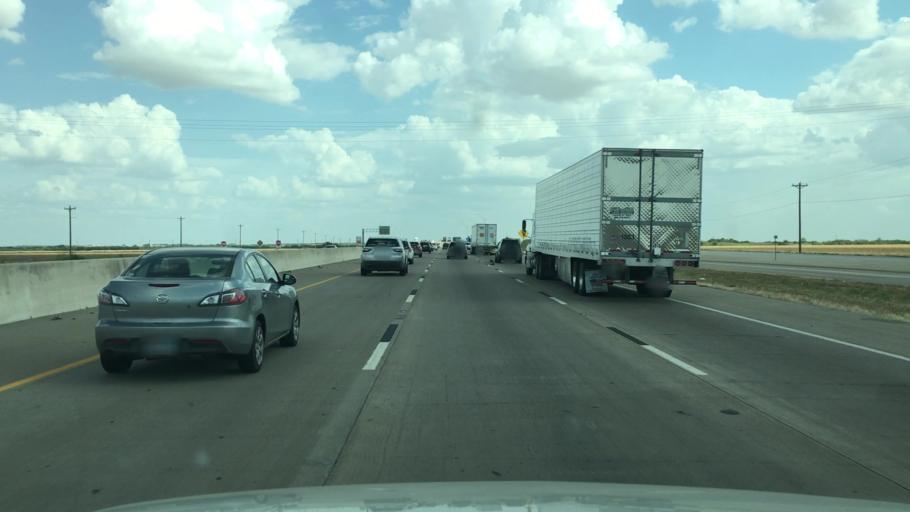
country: US
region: Texas
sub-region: Hill County
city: Hillsboro
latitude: 31.9459
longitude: -97.1106
